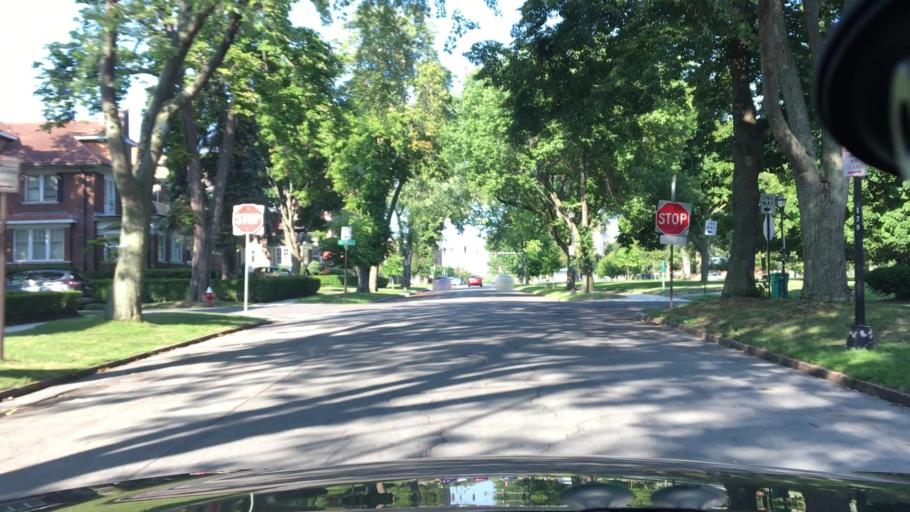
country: US
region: New York
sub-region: Erie County
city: Buffalo
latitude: 42.9021
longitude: -78.8951
